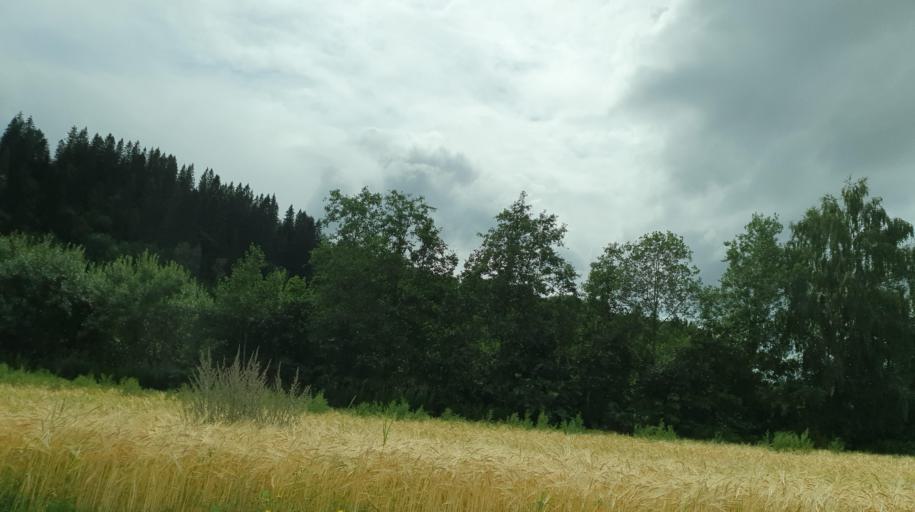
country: NO
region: Nord-Trondelag
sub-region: Stjordal
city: Stjordalshalsen
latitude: 63.4492
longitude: 10.9903
